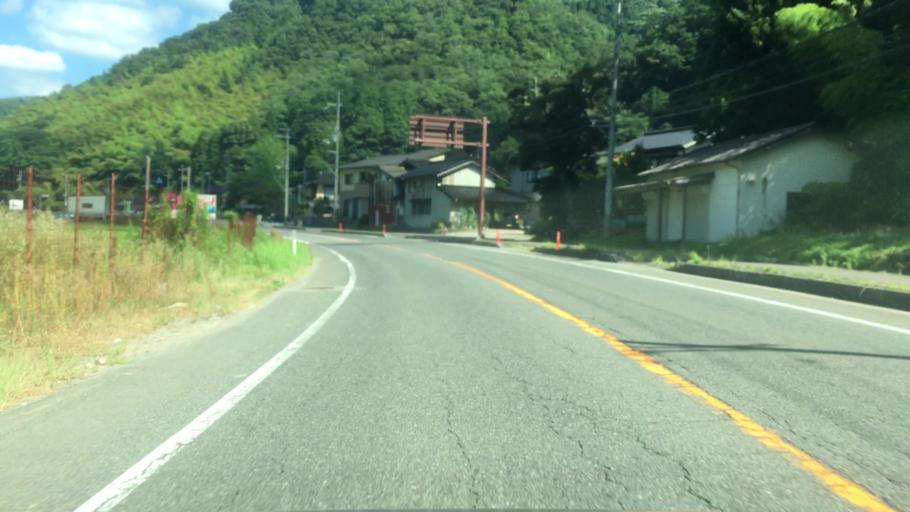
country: JP
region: Hyogo
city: Toyooka
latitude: 35.5698
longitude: 134.7812
